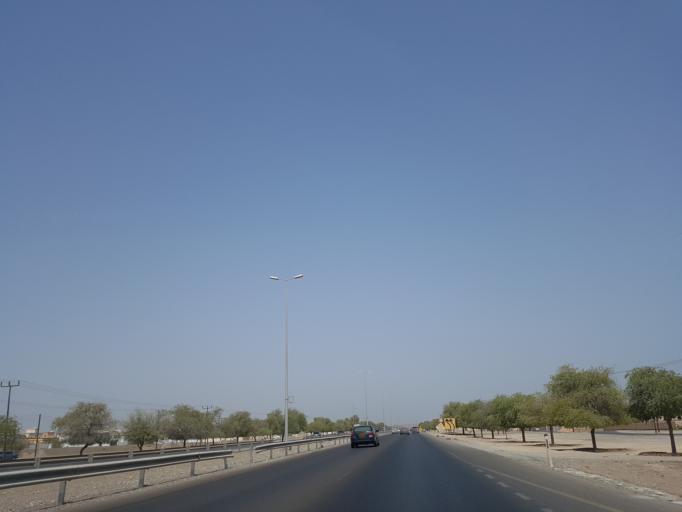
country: OM
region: Al Batinah
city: Saham
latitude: 24.0605
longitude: 56.9628
